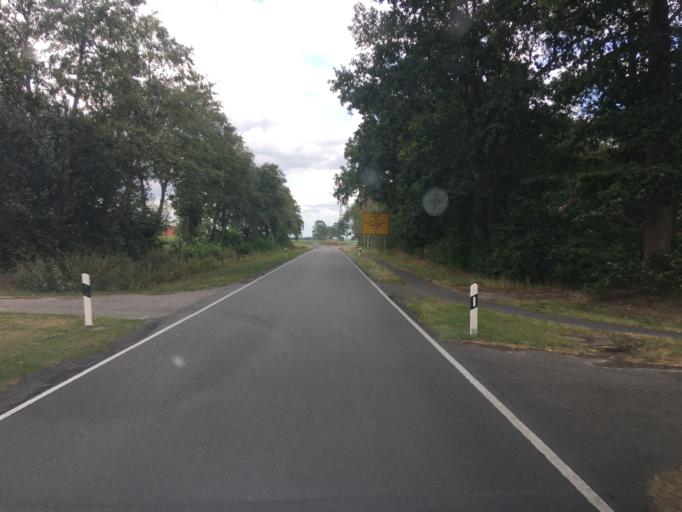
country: DE
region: Lower Saxony
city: Hilkenbrook
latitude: 53.0714
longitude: 7.7148
